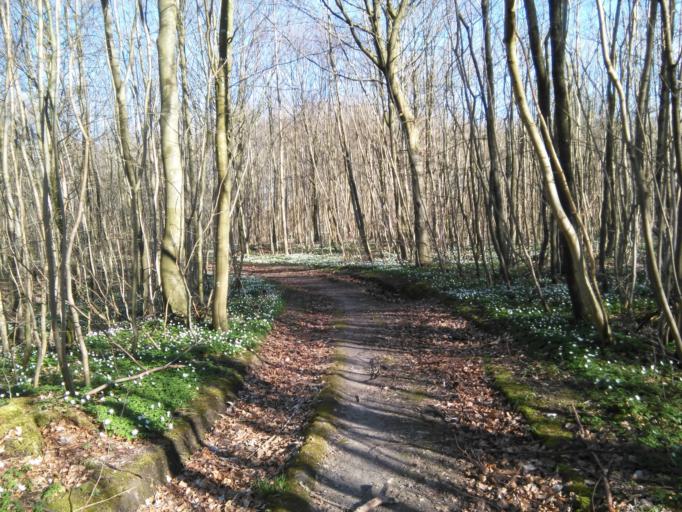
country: DK
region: Central Jutland
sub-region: Arhus Kommune
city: Beder
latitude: 56.0434
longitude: 10.2124
